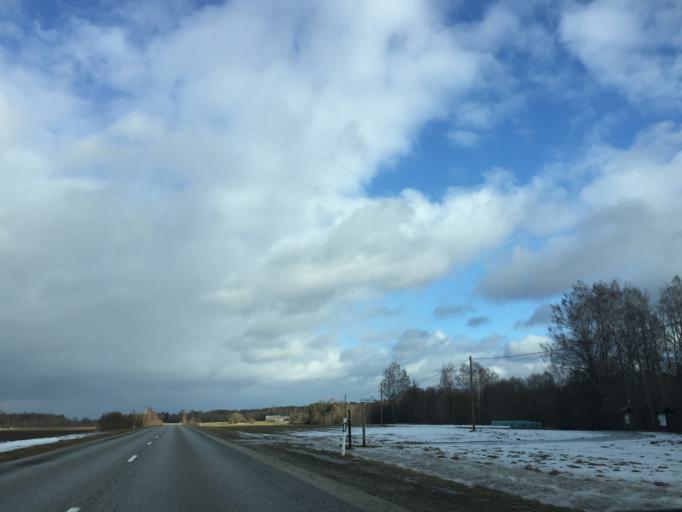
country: LV
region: Aloja
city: Staicele
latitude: 57.8783
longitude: 24.5888
